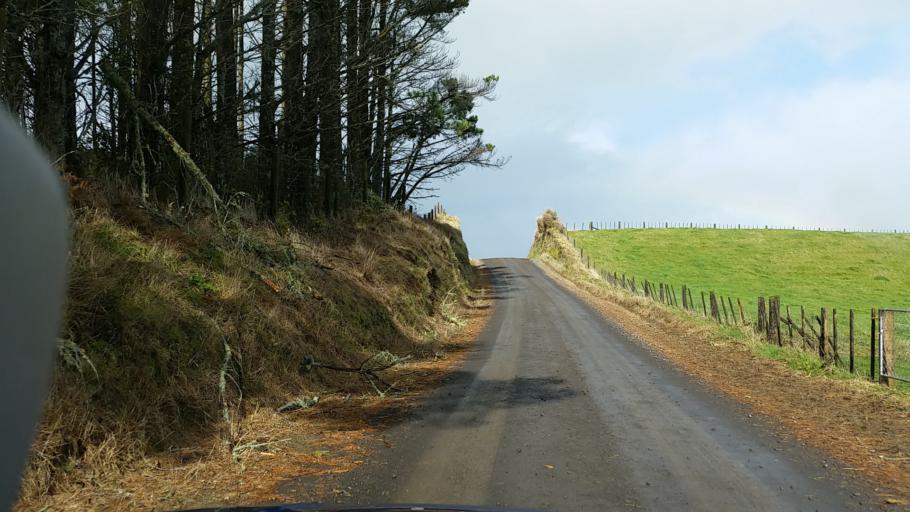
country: NZ
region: Taranaki
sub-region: South Taranaki District
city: Eltham
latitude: -39.2778
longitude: 174.3078
